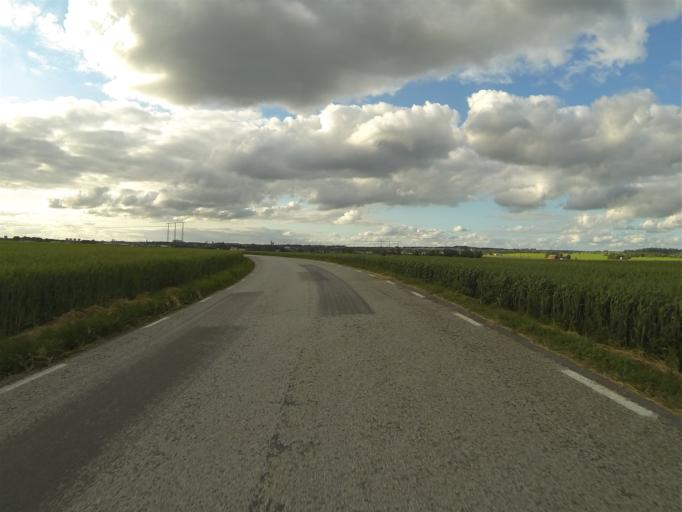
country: SE
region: Skane
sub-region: Staffanstorps Kommun
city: Staffanstorp
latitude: 55.6738
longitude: 13.2325
